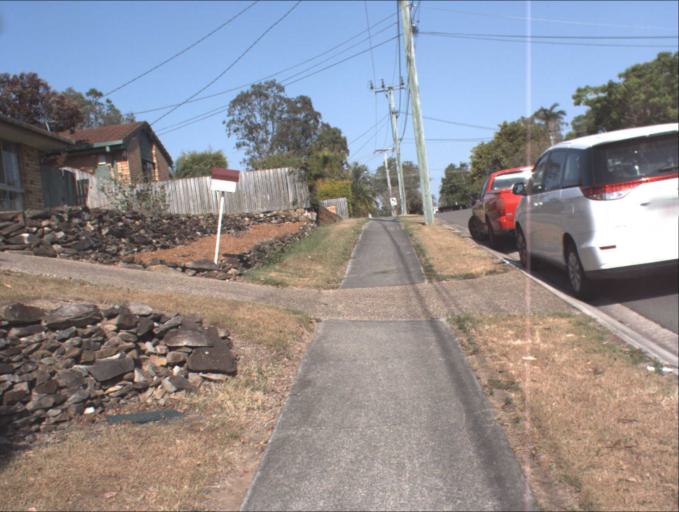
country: AU
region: Queensland
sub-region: Logan
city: Beenleigh
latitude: -27.6945
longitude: 153.1764
